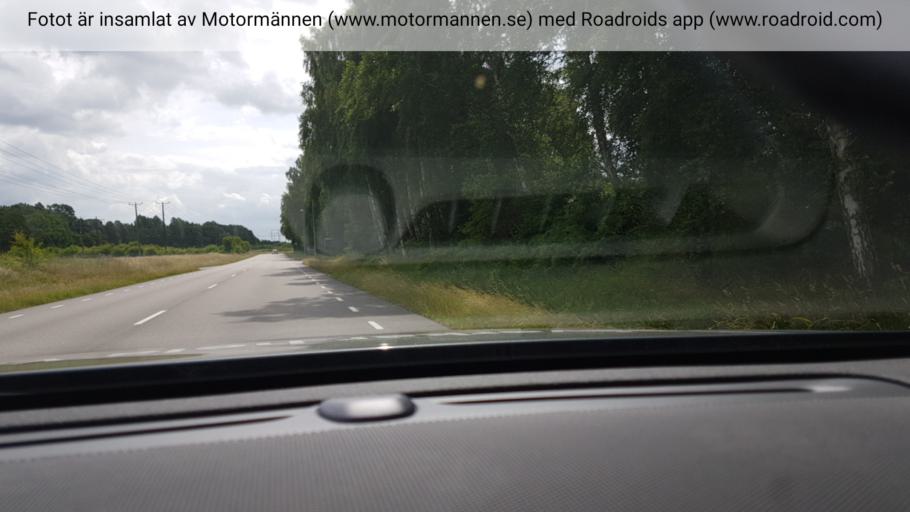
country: SE
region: Skane
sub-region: Hassleholms Kommun
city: Hassleholm
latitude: 56.1746
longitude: 13.7961
